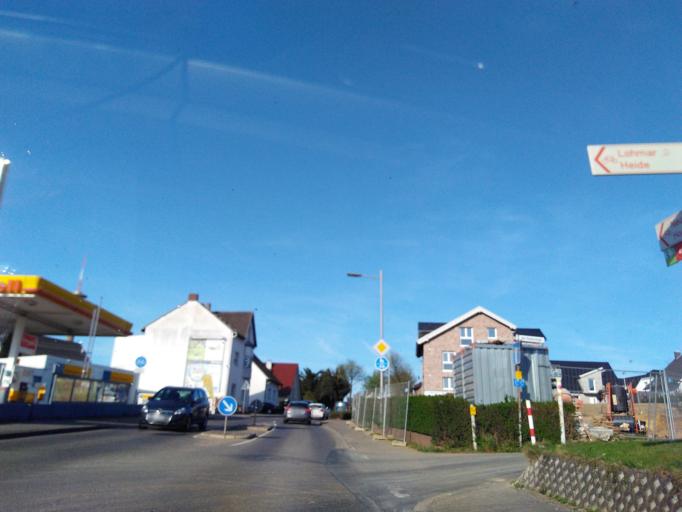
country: DE
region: North Rhine-Westphalia
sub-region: Regierungsbezirk Koln
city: Stossdorf
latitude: 50.8249
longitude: 7.2769
